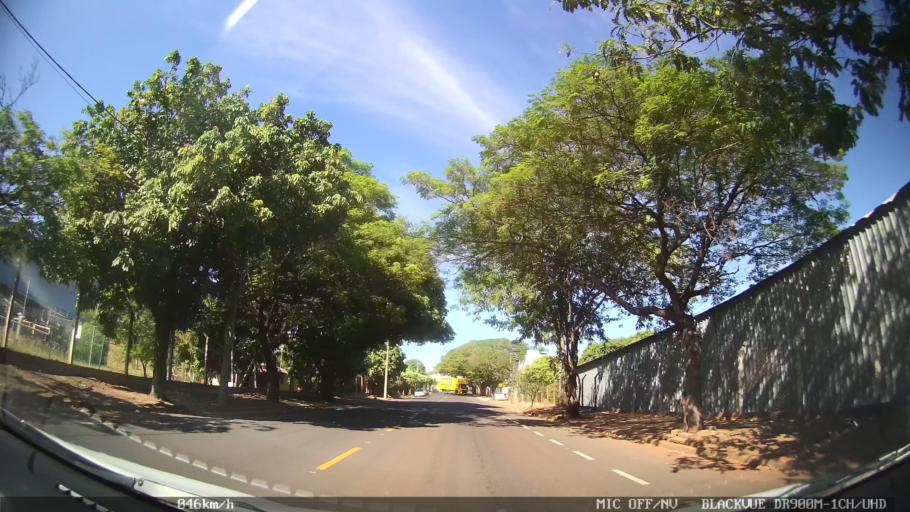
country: BR
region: Sao Paulo
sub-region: Sao Jose Do Rio Preto
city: Sao Jose do Rio Preto
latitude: -20.8103
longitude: -49.4212
